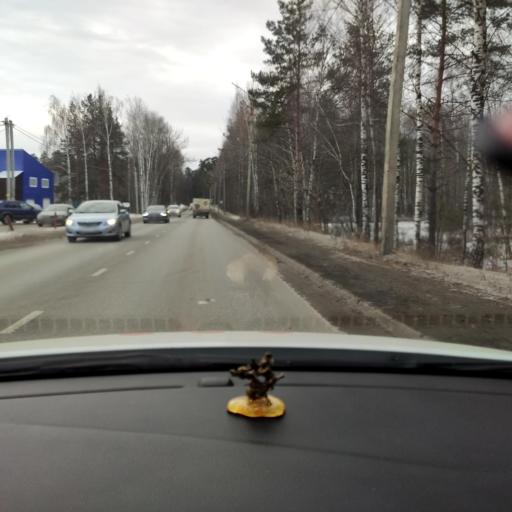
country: RU
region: Tatarstan
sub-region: Zelenodol'skiy Rayon
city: Zelenodolsk
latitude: 55.8656
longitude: 48.5378
